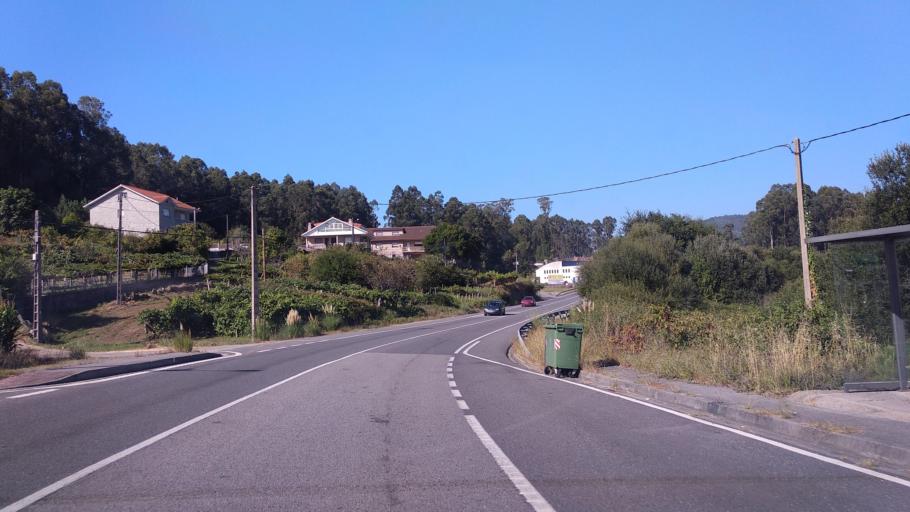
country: ES
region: Galicia
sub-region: Provincia de Pontevedra
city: Marin
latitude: 42.3517
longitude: -8.6418
